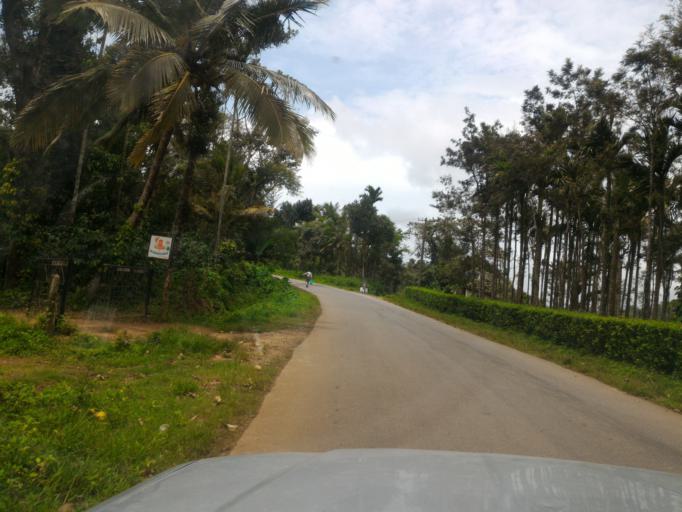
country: IN
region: Karnataka
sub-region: Kodagu
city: Ponnampet
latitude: 12.1004
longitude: 75.9384
